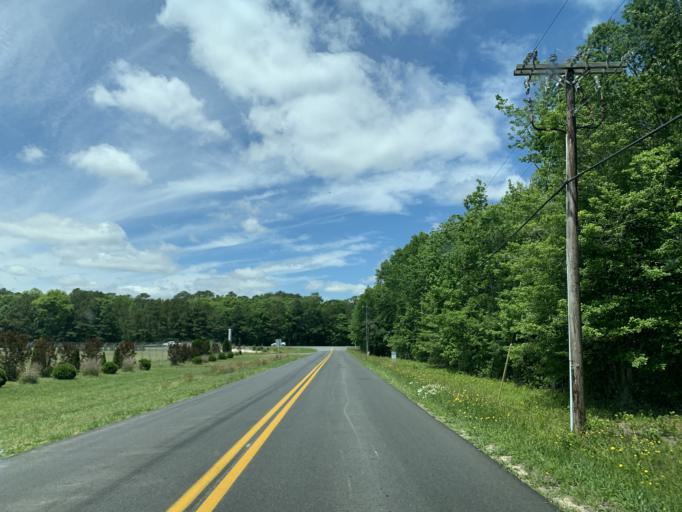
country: US
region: Maryland
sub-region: Worcester County
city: West Ocean City
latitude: 38.3182
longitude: -75.1238
